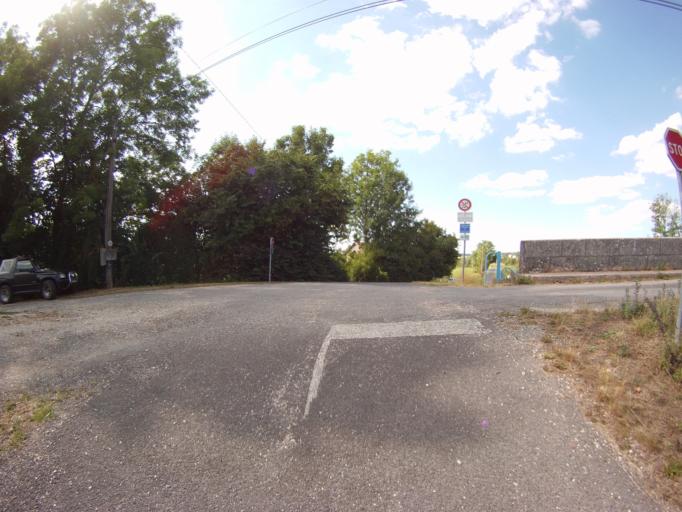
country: FR
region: Lorraine
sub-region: Departement de la Meuse
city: Longeville-en-Barrois
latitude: 48.7515
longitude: 5.1938
